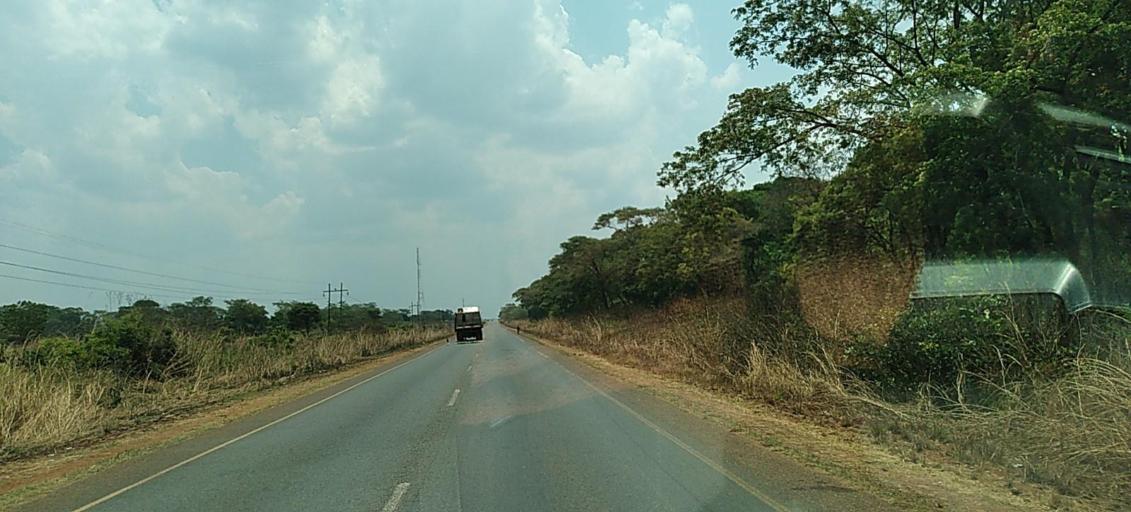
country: ZM
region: Copperbelt
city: Kalulushi
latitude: -12.8400
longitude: 27.9958
